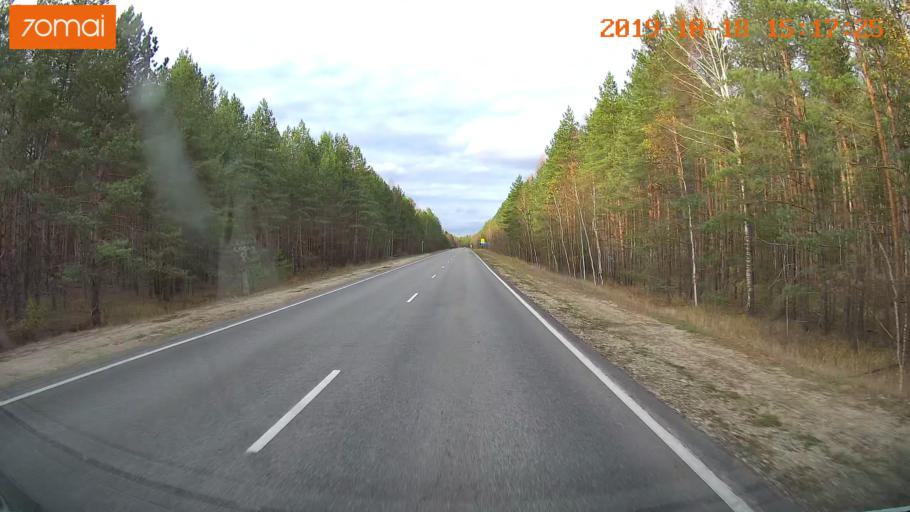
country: RU
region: Vladimir
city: Anopino
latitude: 55.6494
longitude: 40.7265
